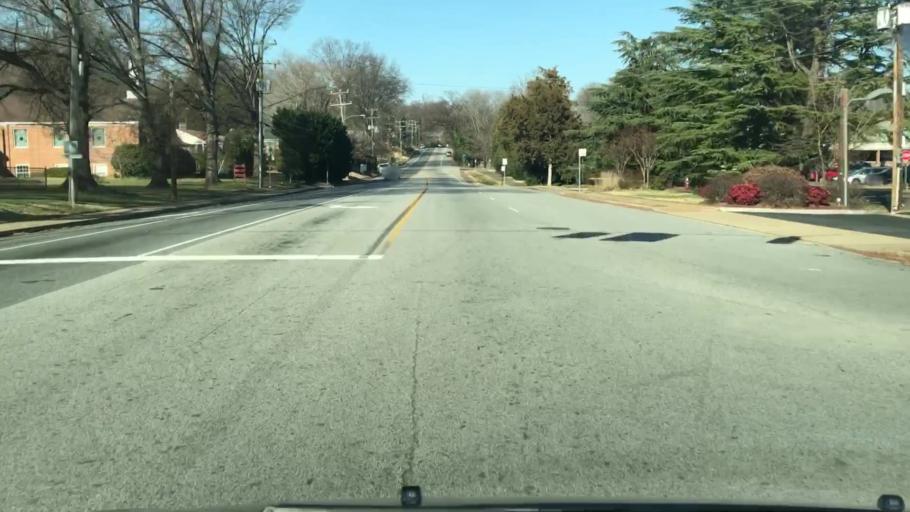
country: US
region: Virginia
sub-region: Fairfax County
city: Belle Haven
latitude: 38.7752
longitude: -77.0626
